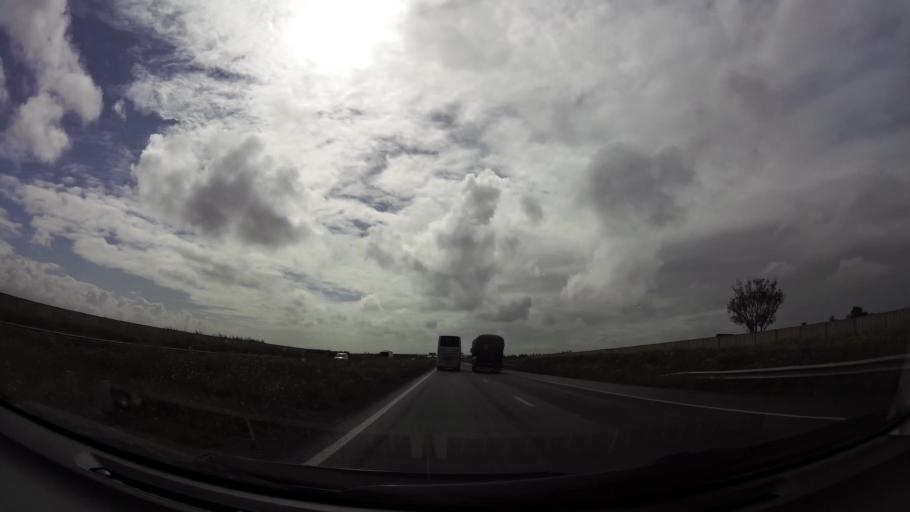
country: MA
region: Grand Casablanca
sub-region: Nouaceur
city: Dar Bouazza
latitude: 33.3536
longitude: -7.9689
